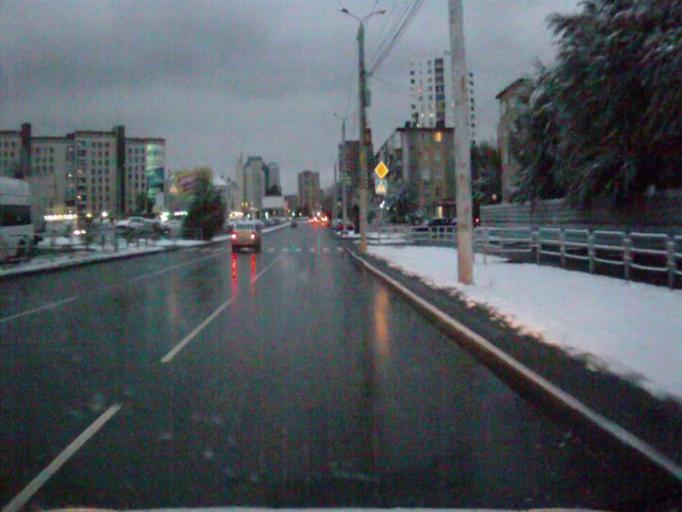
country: RU
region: Chelyabinsk
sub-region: Gorod Chelyabinsk
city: Chelyabinsk
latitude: 55.1485
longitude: 61.3933
